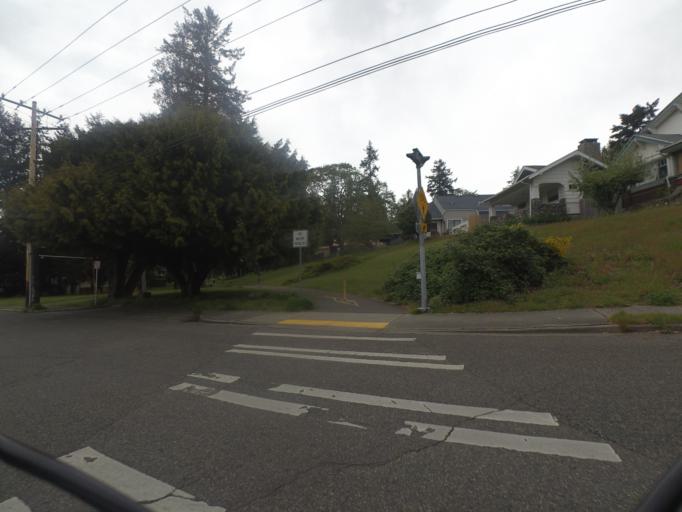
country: US
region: Washington
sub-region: Pierce County
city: Fircrest
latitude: 47.2078
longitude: -122.4789
